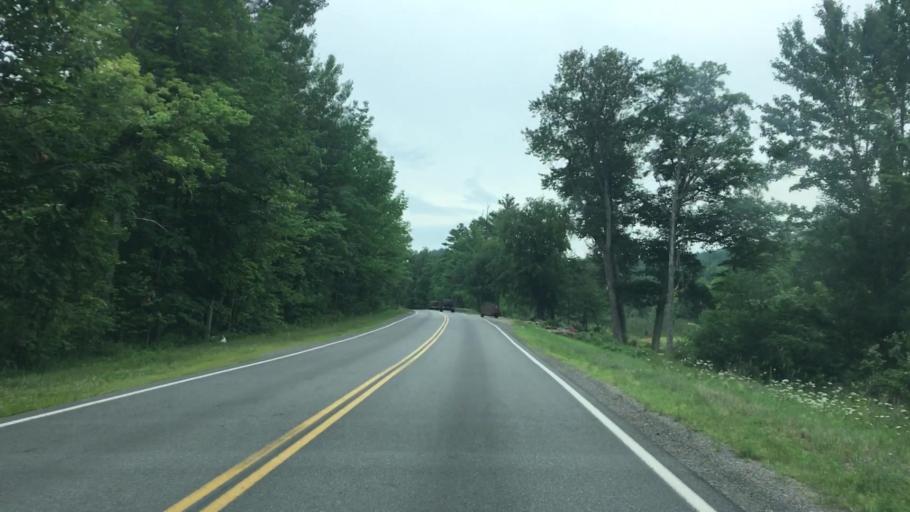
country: US
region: New York
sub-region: Clinton County
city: Peru
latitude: 44.5013
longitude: -73.5894
